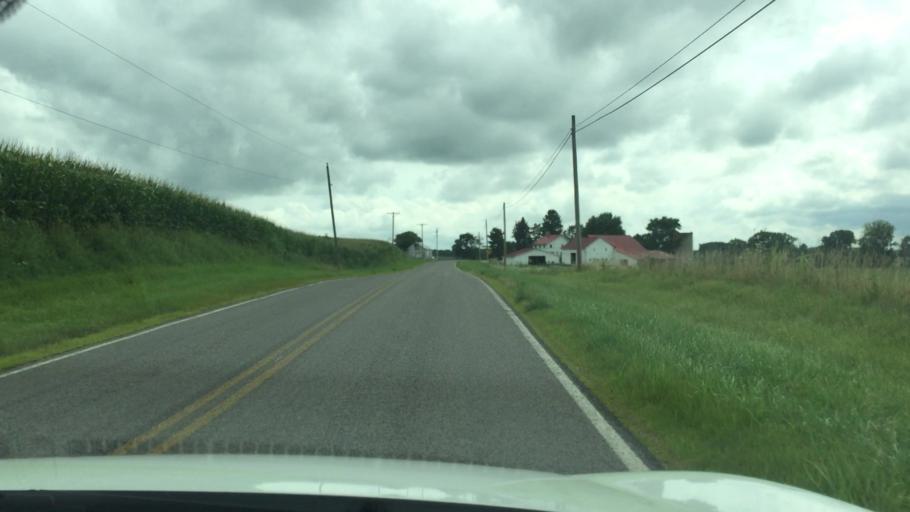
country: US
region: Ohio
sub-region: Champaign County
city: Mechanicsburg
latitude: 40.0682
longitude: -83.6483
